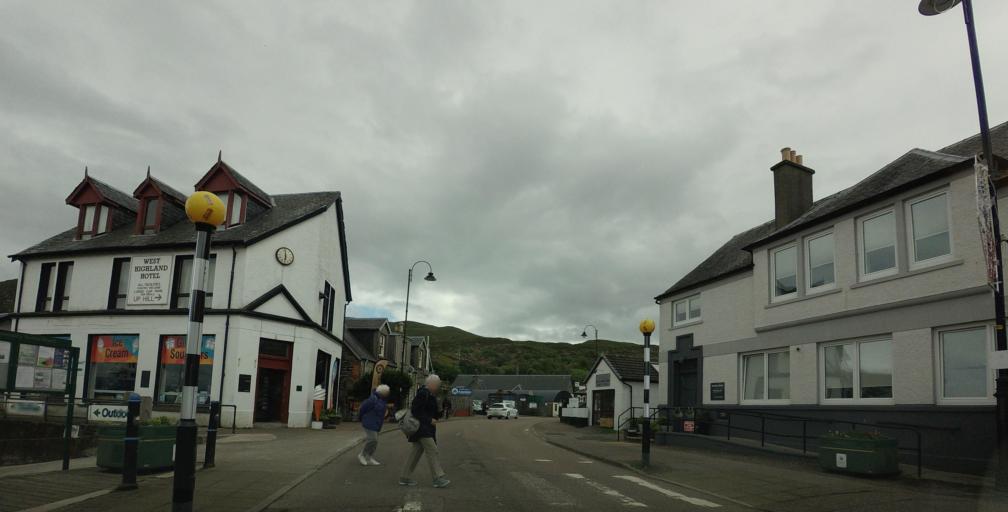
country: GB
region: Scotland
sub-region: Highland
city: Portree
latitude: 57.0054
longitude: -5.8287
